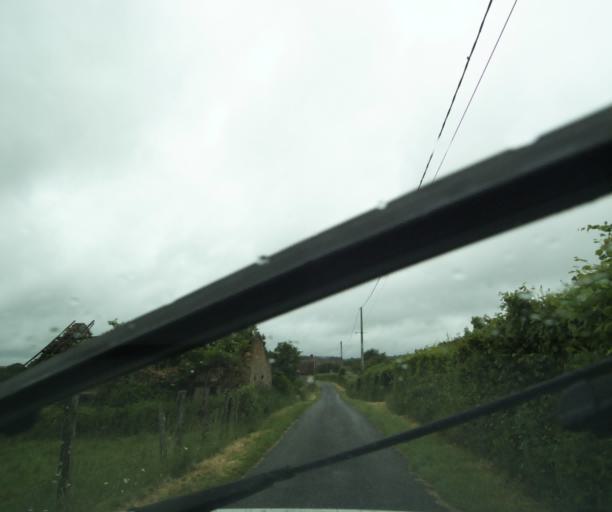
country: FR
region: Bourgogne
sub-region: Departement de Saone-et-Loire
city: Charolles
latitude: 46.4814
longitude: 4.4127
